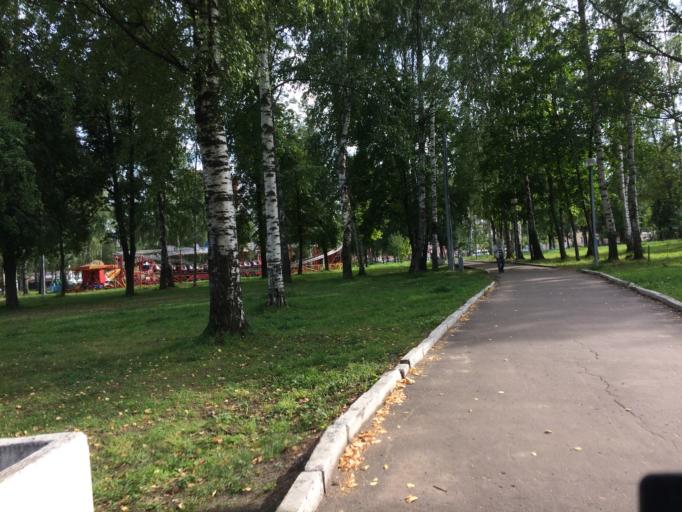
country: RU
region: Mariy-El
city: Yoshkar-Ola
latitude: 56.6397
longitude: 47.8676
